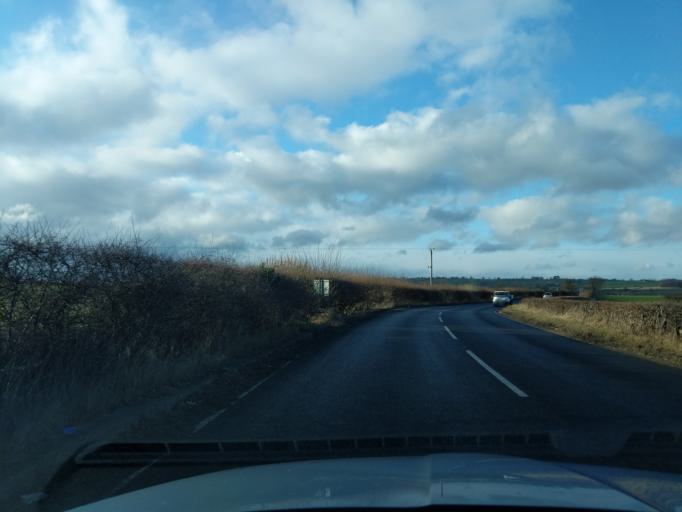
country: GB
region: England
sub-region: North Yorkshire
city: Catterick
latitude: 54.3180
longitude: -1.6763
